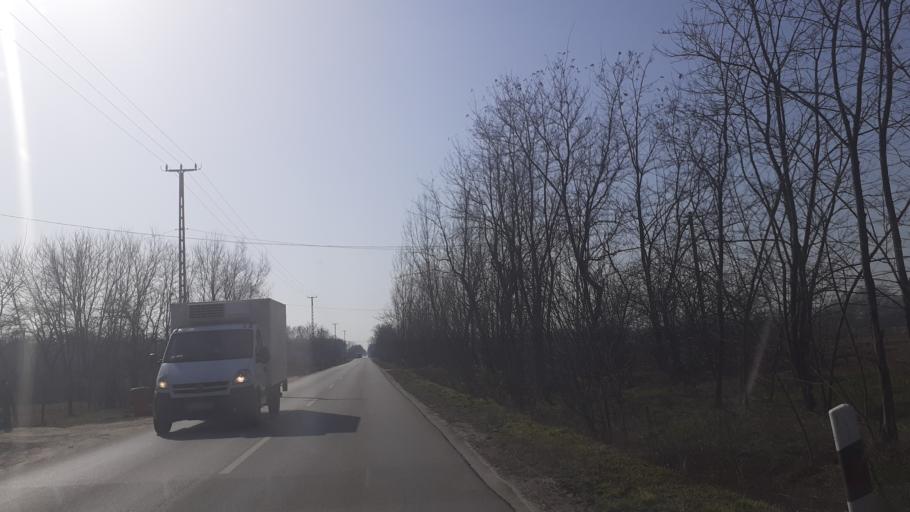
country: HU
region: Bacs-Kiskun
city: Lajosmizse
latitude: 47.0131
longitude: 19.5124
